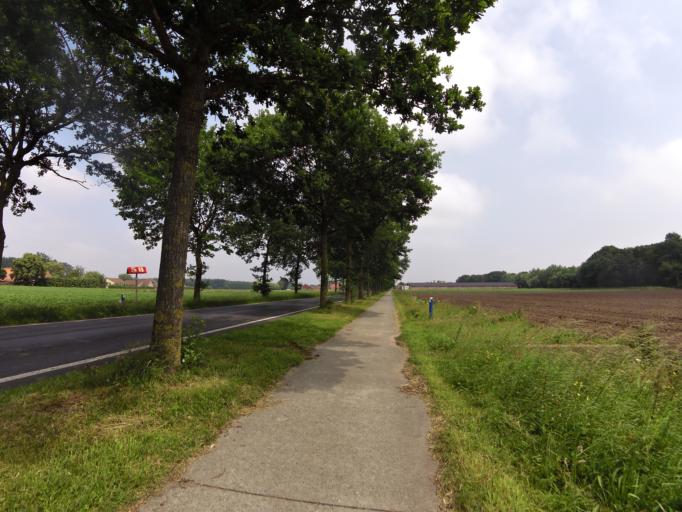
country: BE
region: Flanders
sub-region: Provincie West-Vlaanderen
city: Jabbeke
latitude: 51.1474
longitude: 3.0763
